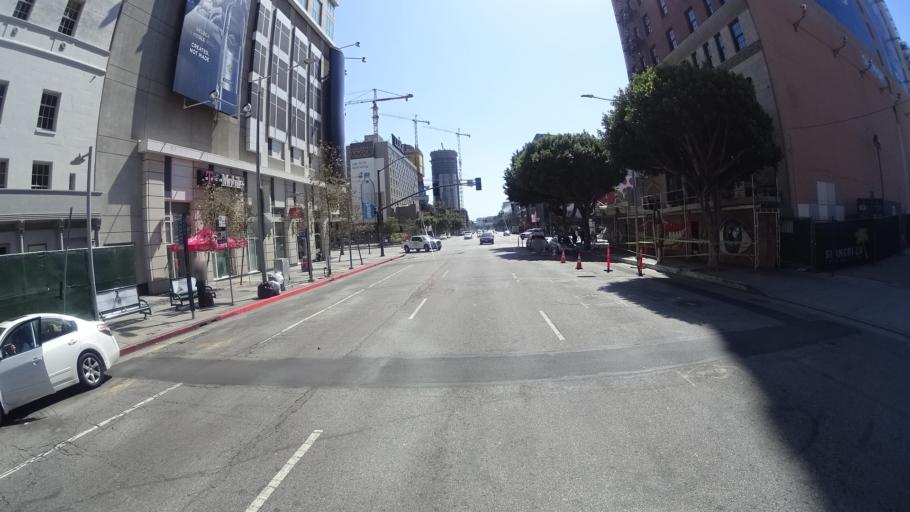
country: US
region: California
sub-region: Los Angeles County
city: Los Angeles
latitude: 34.0454
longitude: -118.2635
